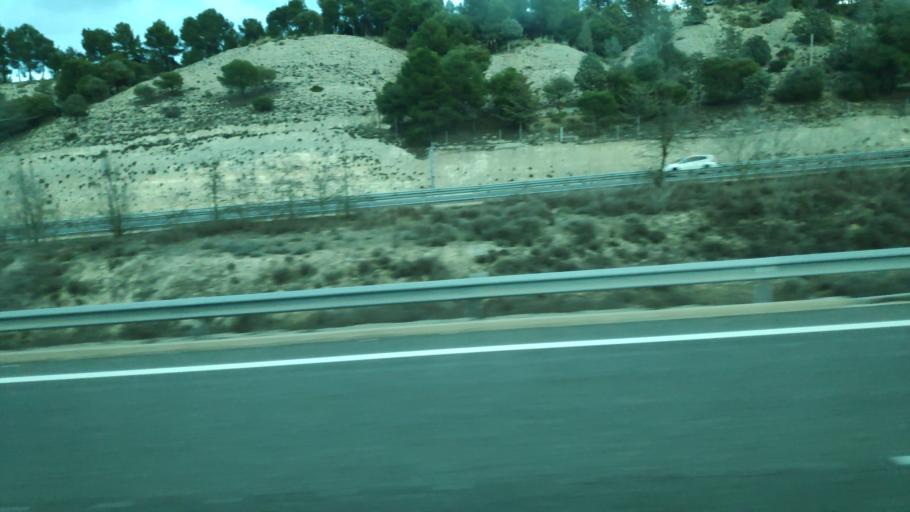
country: ES
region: Castille-La Mancha
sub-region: Provincia de Cuenca
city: Belinchon
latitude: 40.0238
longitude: -3.0355
